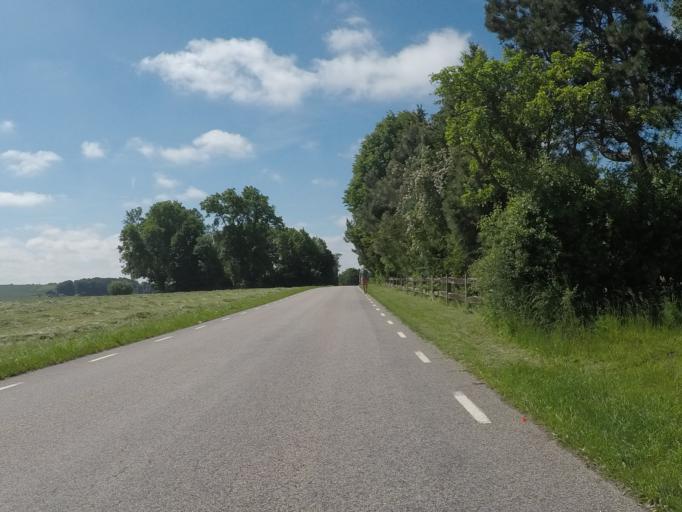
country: SE
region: Skane
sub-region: Staffanstorps Kommun
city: Staffanstorp
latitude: 55.6205
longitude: 13.2170
